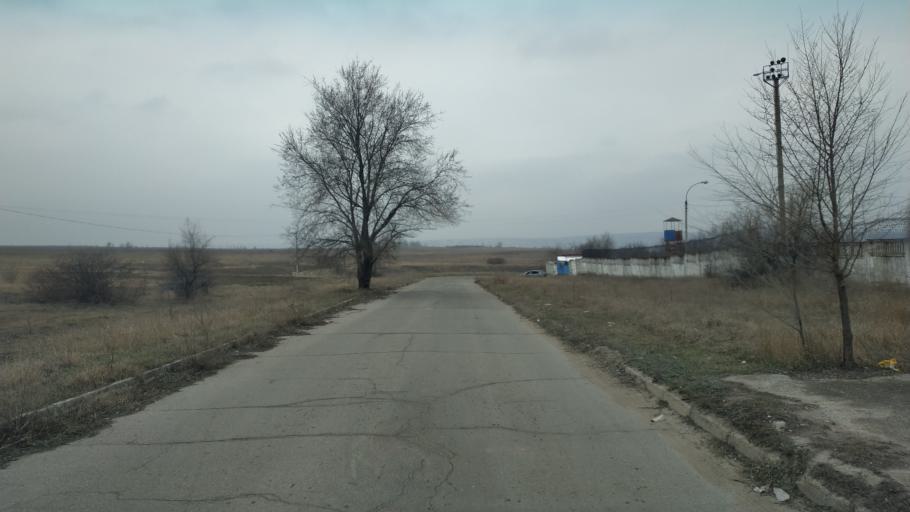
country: MD
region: Chisinau
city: Singera
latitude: 46.9140
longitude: 29.0047
